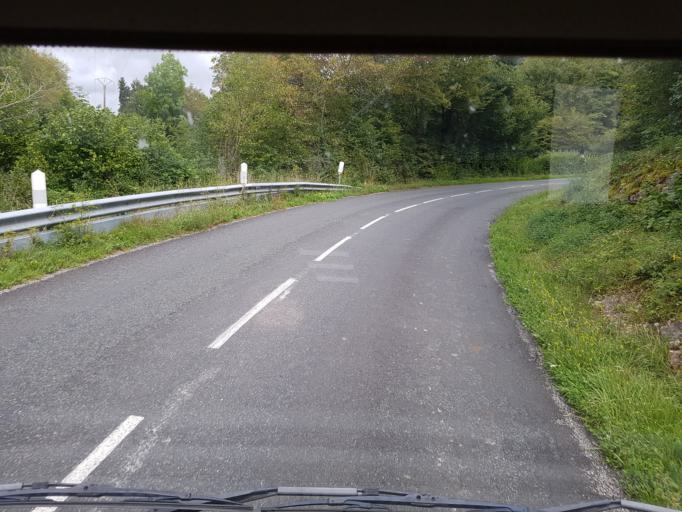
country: FR
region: Rhone-Alpes
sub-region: Departement de l'Ain
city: Saint-Martin-du-Frene
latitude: 46.1125
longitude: 5.4900
